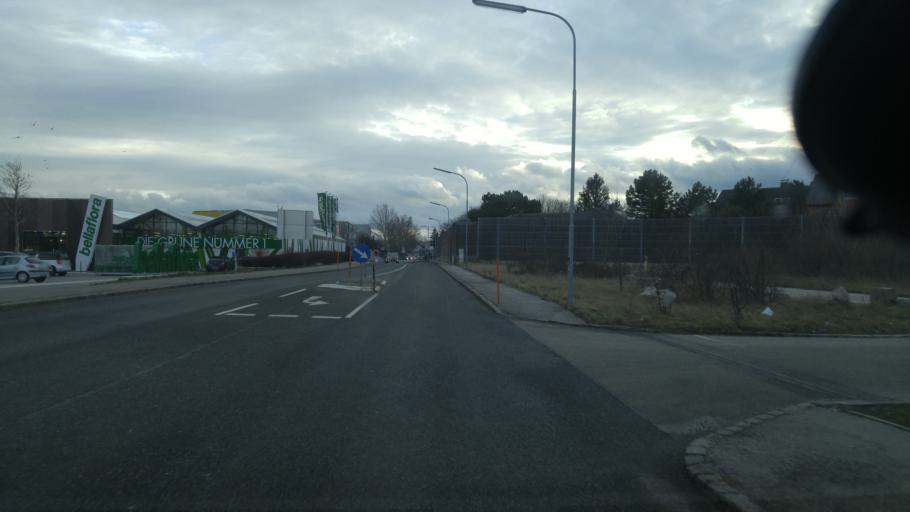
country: AT
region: Lower Austria
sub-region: Politischer Bezirk Baden
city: Bad Voslau
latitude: 47.9763
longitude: 16.2216
